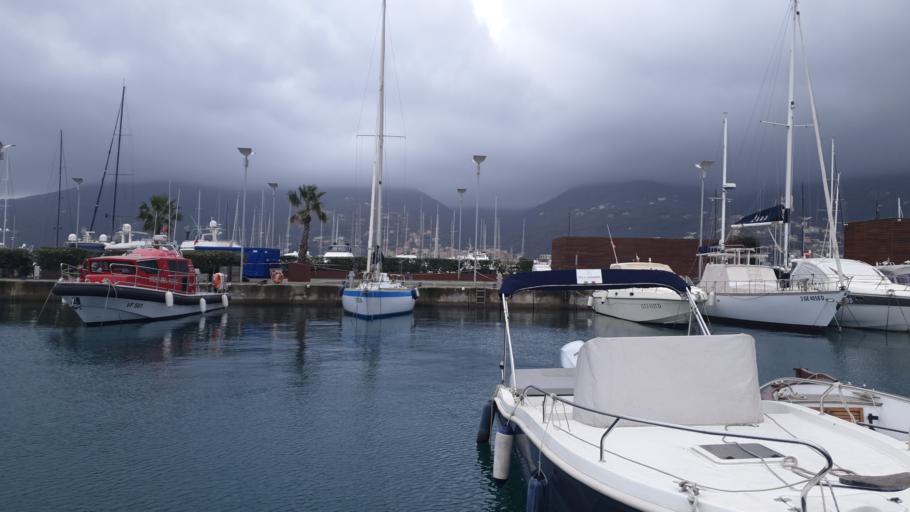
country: IT
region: Liguria
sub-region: Provincia di La Spezia
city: La Spezia
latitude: 44.0995
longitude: 9.8320
